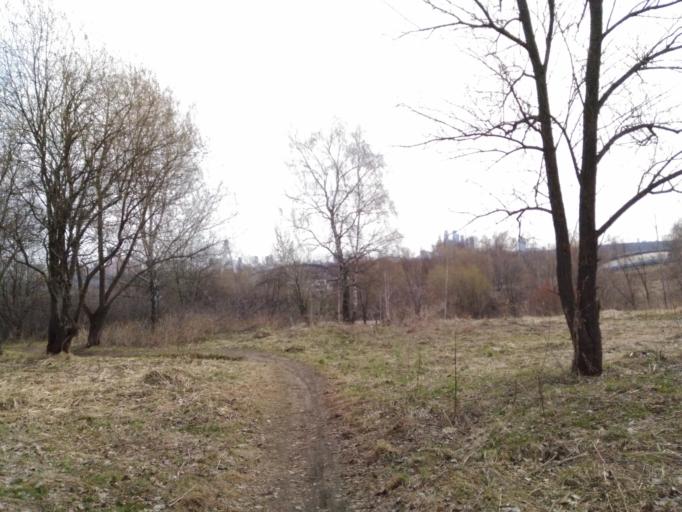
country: RU
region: Moscow
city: Shchukino
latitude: 55.7661
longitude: 37.4249
